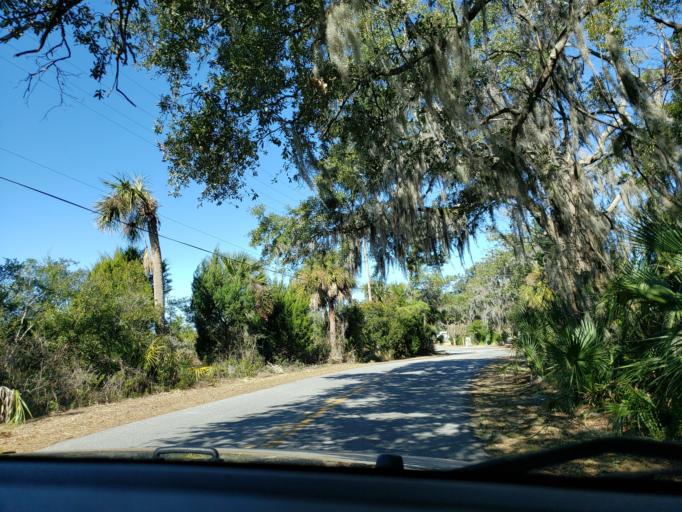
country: US
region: Georgia
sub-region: Chatham County
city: Whitemarsh Island
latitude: 32.0519
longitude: -81.0088
